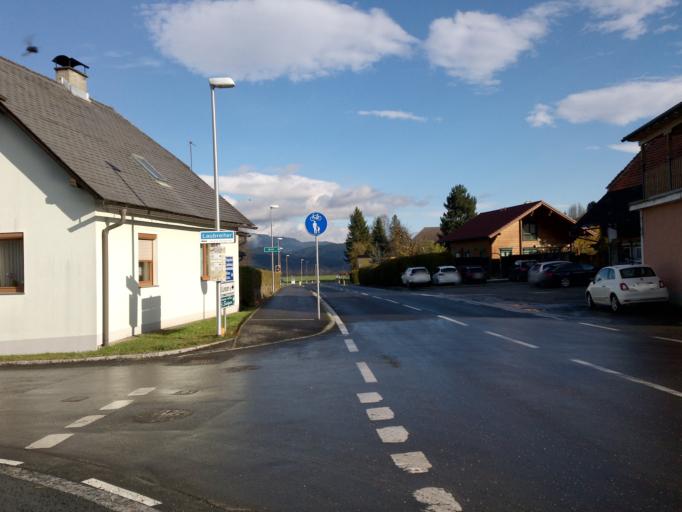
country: AT
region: Styria
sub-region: Politischer Bezirk Murtal
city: Sankt Margarethen bei Knittelfeld
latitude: 47.2271
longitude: 14.8591
